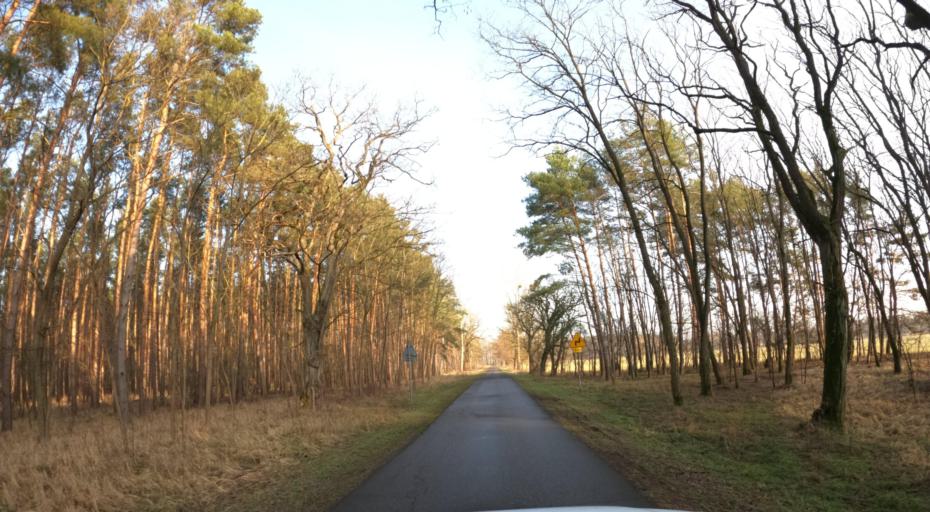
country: PL
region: West Pomeranian Voivodeship
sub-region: Powiat mysliborski
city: Boleszkowice
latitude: 52.6685
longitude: 14.5158
